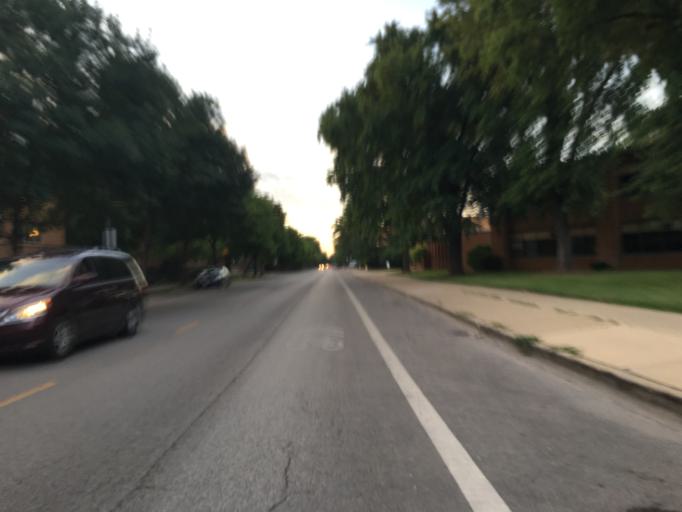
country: US
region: Illinois
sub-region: Cook County
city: Lincolnwood
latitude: 41.9476
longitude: -87.6980
